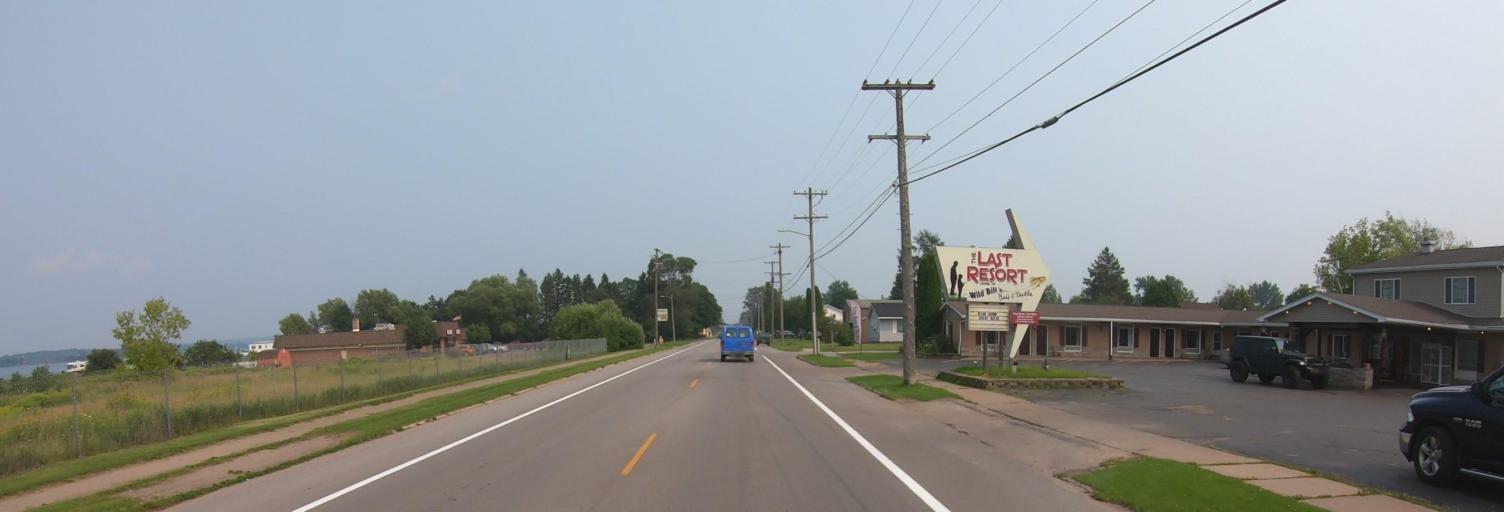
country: US
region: Michigan
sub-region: Chippewa County
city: Sault Ste. Marie
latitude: 46.4910
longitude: -84.3182
